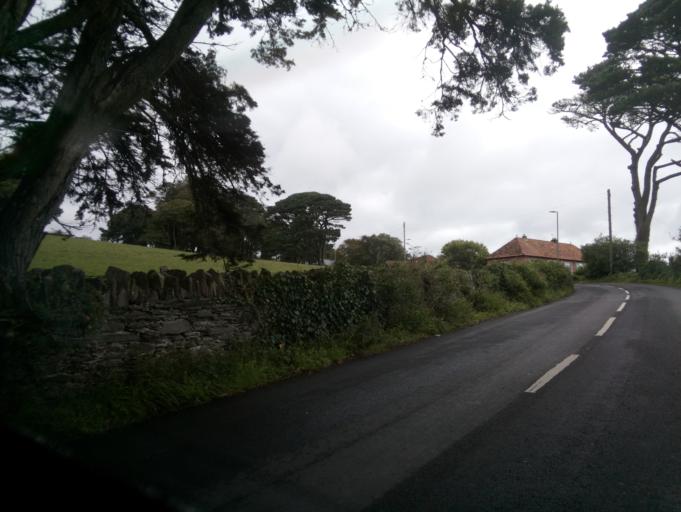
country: GB
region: England
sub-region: Devon
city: Dartmouth
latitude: 50.3210
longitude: -3.5992
